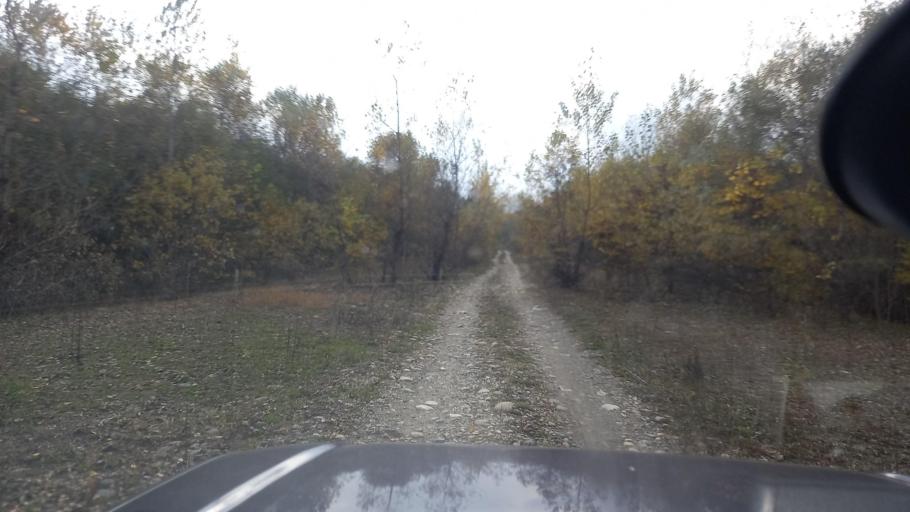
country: RU
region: Krasnodarskiy
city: Shedok
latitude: 44.1721
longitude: 40.8480
